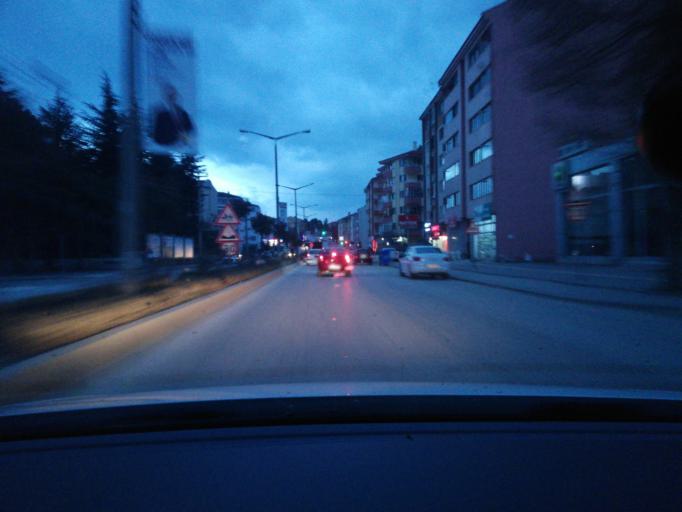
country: TR
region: Bolu
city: Bolu
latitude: 40.7367
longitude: 31.6186
